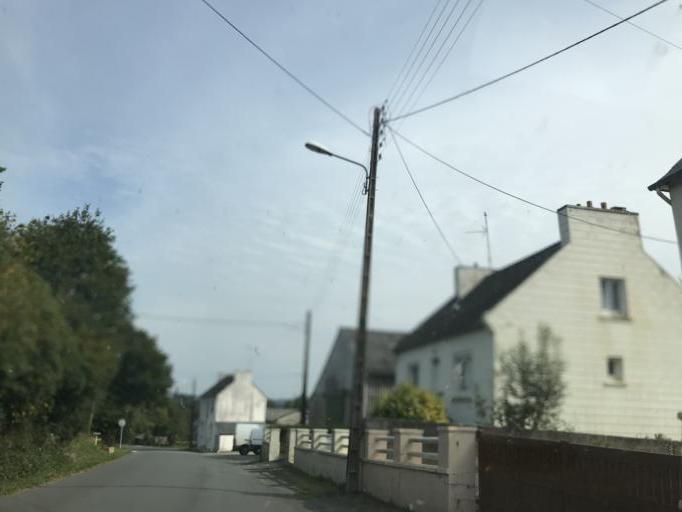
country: FR
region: Brittany
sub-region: Departement du Finistere
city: Brasparts
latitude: 48.3028
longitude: -3.9527
